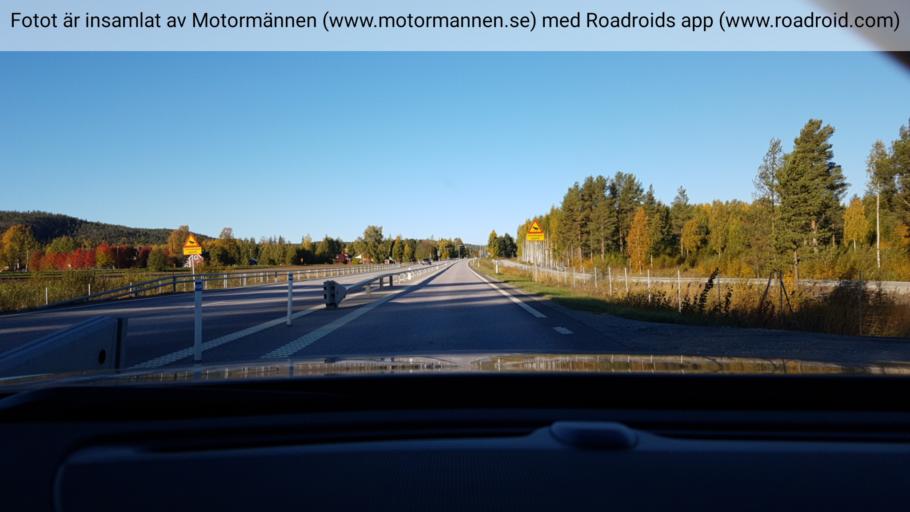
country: SE
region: Norrbotten
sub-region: Pitea Kommun
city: Bergsviken
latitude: 65.3147
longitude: 21.3430
